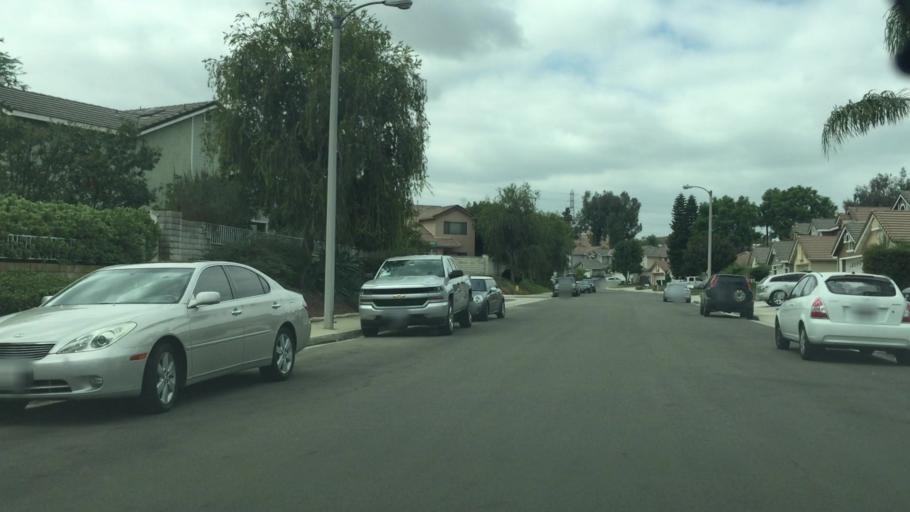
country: US
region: California
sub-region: San Bernardino County
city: Los Serranos
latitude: 33.9345
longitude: -117.6733
